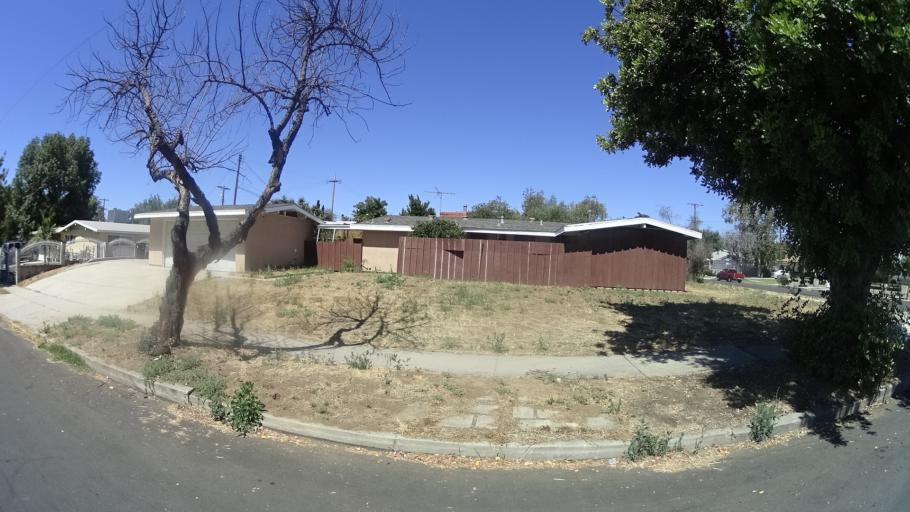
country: US
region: California
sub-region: Los Angeles County
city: San Fernando
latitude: 34.2534
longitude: -118.4544
